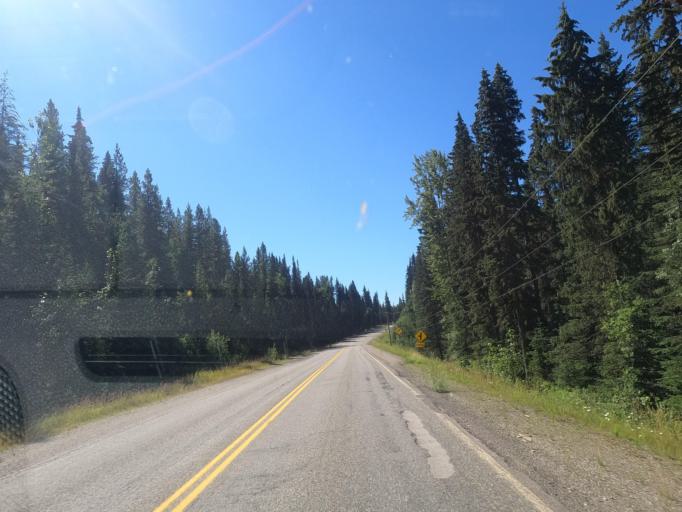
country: CA
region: British Columbia
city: Quesnel
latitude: 53.0375
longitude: -122.2613
